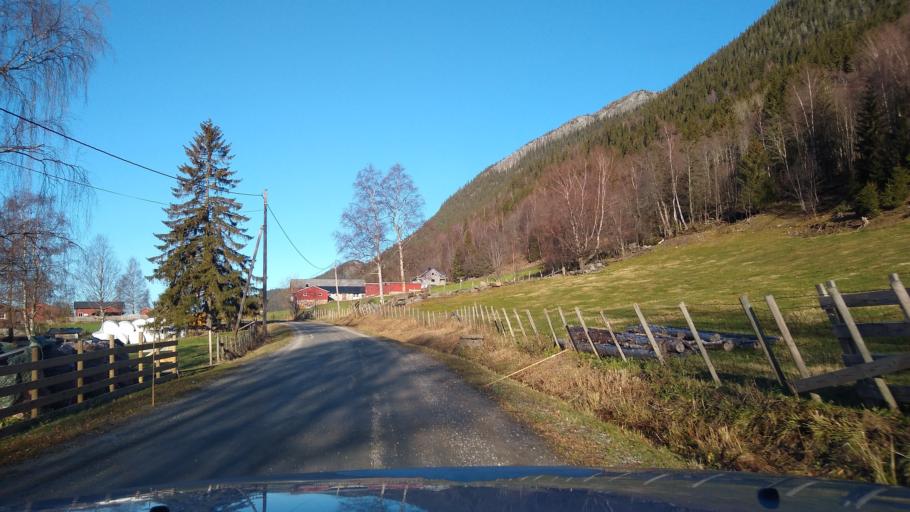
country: NO
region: Oppland
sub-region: Oyer
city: Tretten
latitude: 61.4116
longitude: 10.2414
